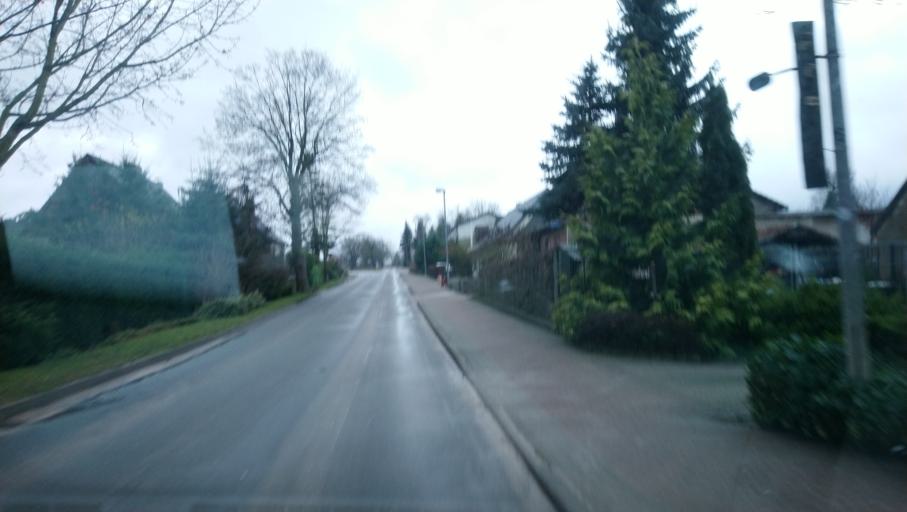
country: DE
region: Mecklenburg-Vorpommern
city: Seehof
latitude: 53.6811
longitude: 11.4288
